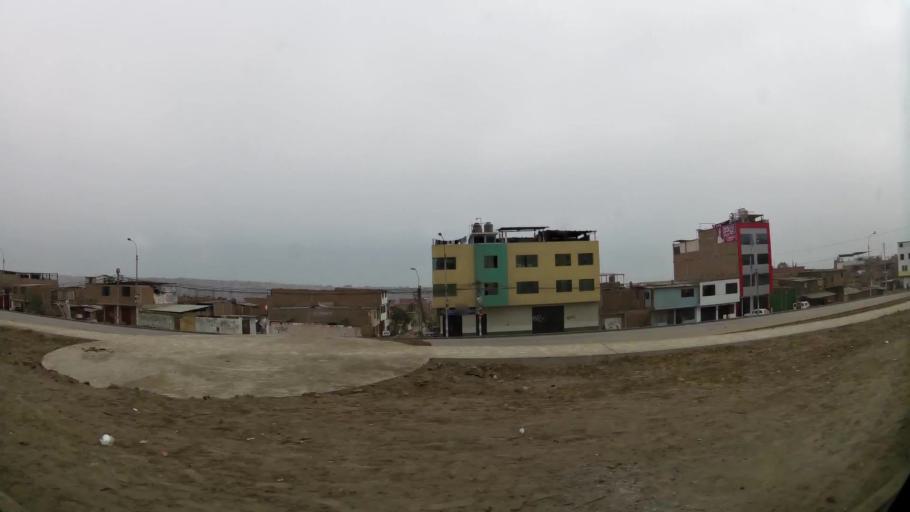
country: PE
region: Lima
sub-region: Lima
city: Surco
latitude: -12.2164
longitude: -76.9464
